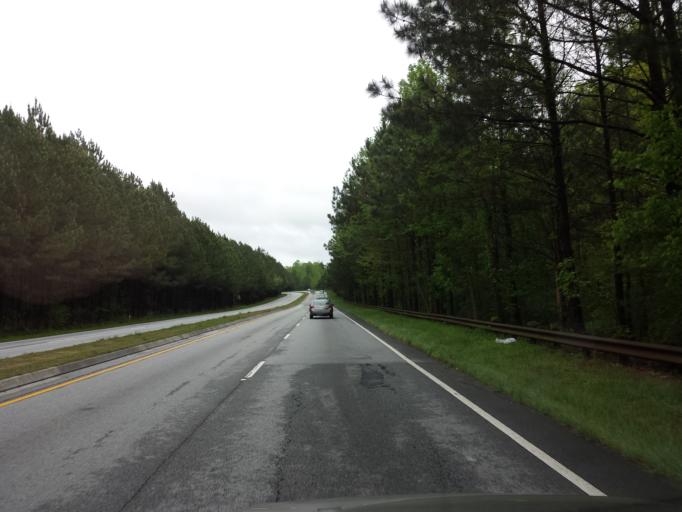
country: US
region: Georgia
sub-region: Cobb County
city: Mableton
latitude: 33.8475
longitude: -84.5506
